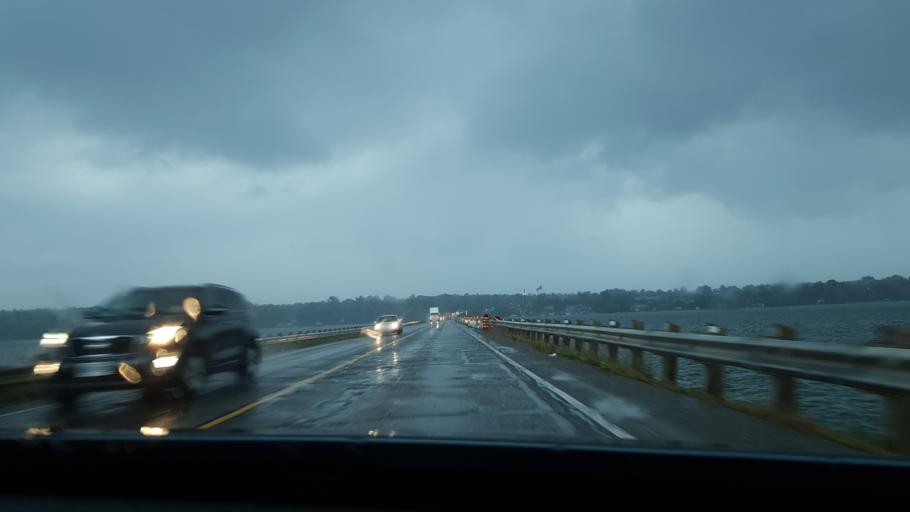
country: CA
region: Ontario
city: Peterborough
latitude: 44.3878
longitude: -78.3960
